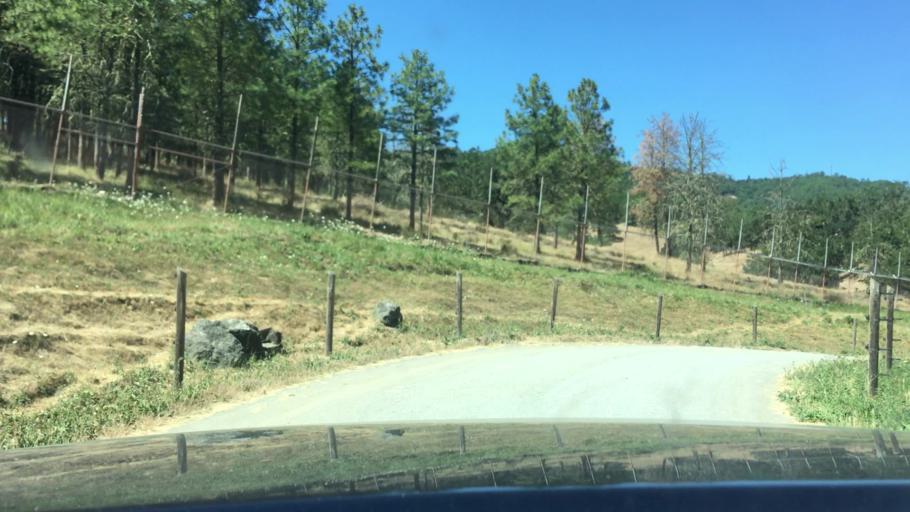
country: US
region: Oregon
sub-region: Douglas County
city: Winston
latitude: 43.1323
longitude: -123.4382
